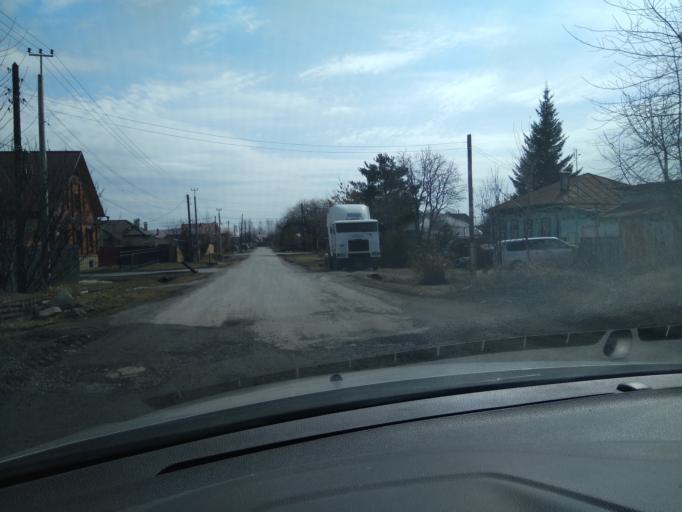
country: RU
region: Sverdlovsk
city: Shuvakish
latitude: 56.8898
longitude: 60.4853
